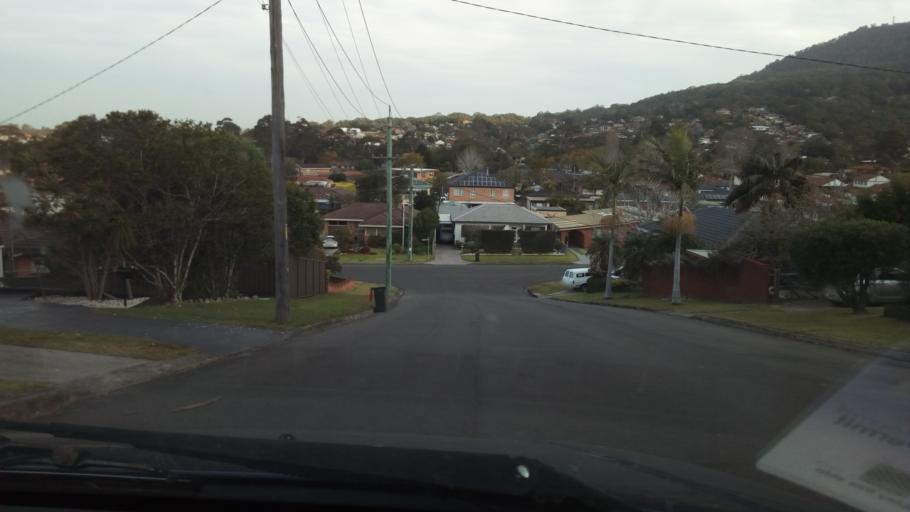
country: AU
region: New South Wales
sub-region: Wollongong
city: Mount Ousley
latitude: -34.3834
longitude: 150.8767
